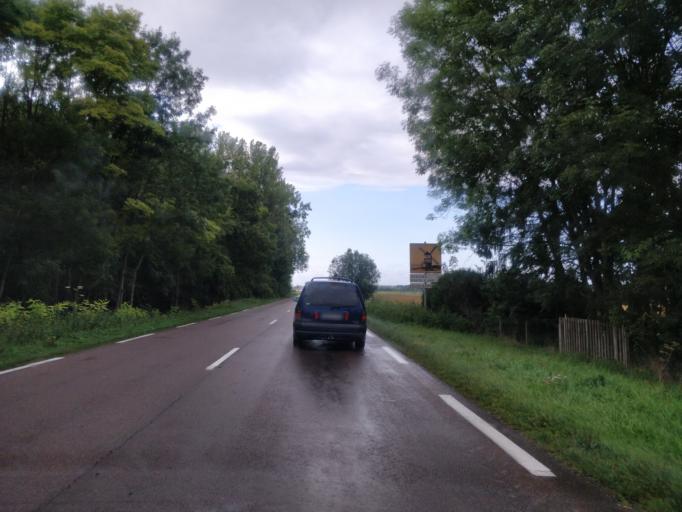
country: FR
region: Champagne-Ardenne
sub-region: Departement de l'Aube
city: Lusigny-sur-Barse
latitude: 48.2582
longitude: 4.2524
